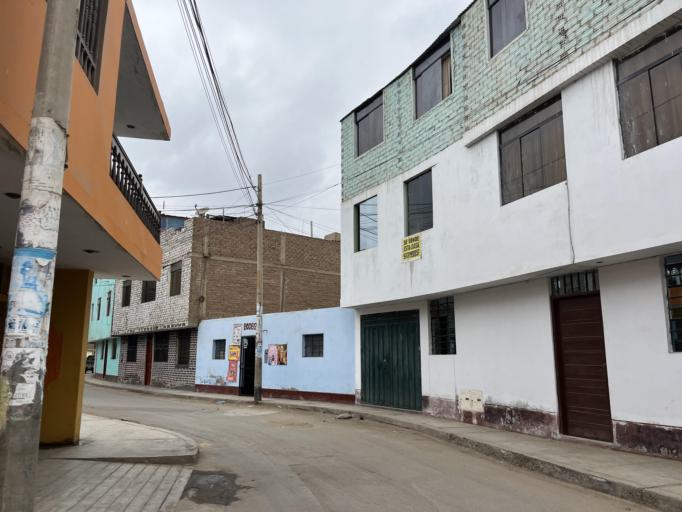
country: PE
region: La Libertad
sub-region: Provincia de Trujillo
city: Trujillo
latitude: -8.1148
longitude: -79.0063
